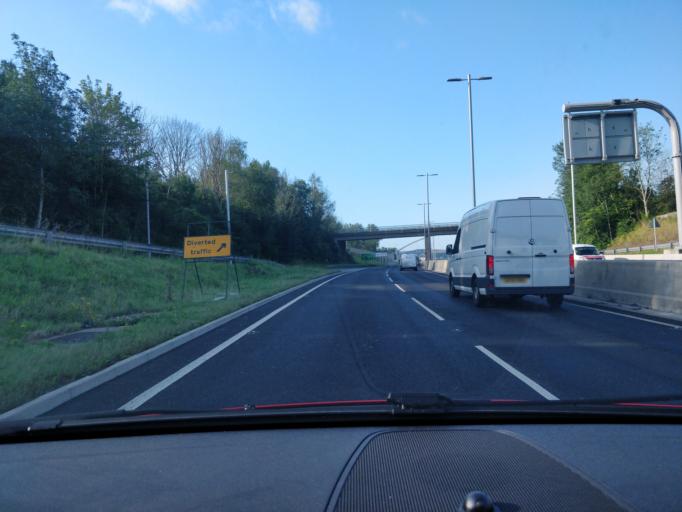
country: GB
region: England
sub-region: Borough of Halton
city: Halton
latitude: 53.3281
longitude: -2.7038
